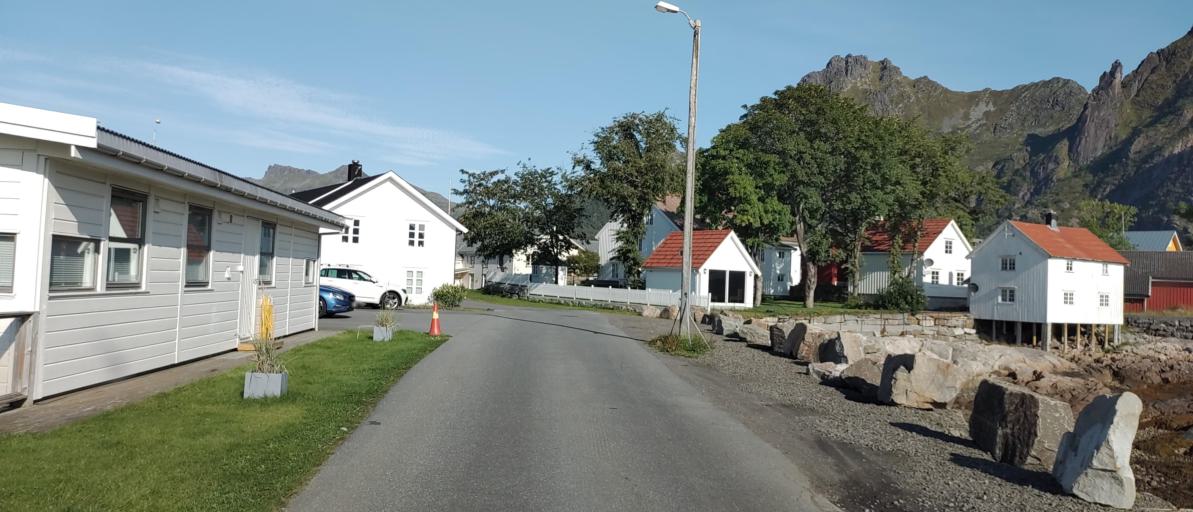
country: NO
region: Nordland
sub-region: Vagan
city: Svolvaer
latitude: 68.2335
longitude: 14.5805
